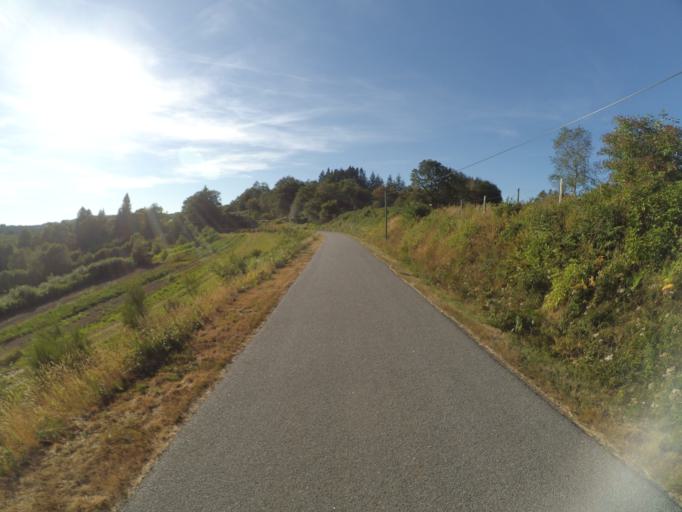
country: FR
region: Limousin
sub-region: Departement de la Creuse
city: Banize
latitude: 45.7610
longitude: 2.0279
